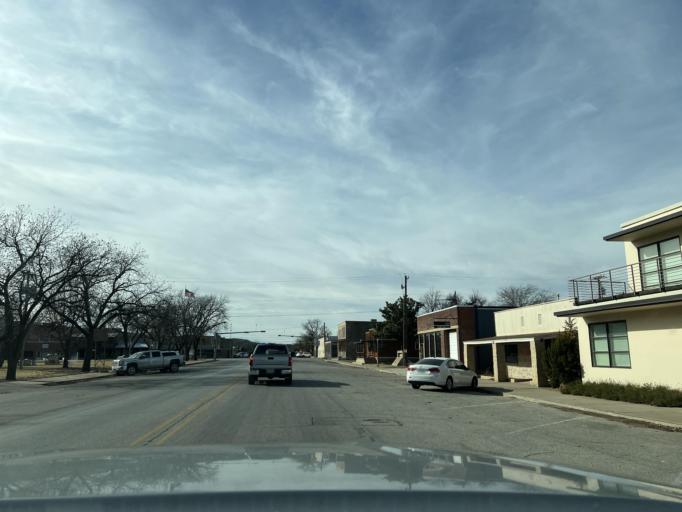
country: US
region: Texas
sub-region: Shackelford County
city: Albany
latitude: 32.7235
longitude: -99.2959
